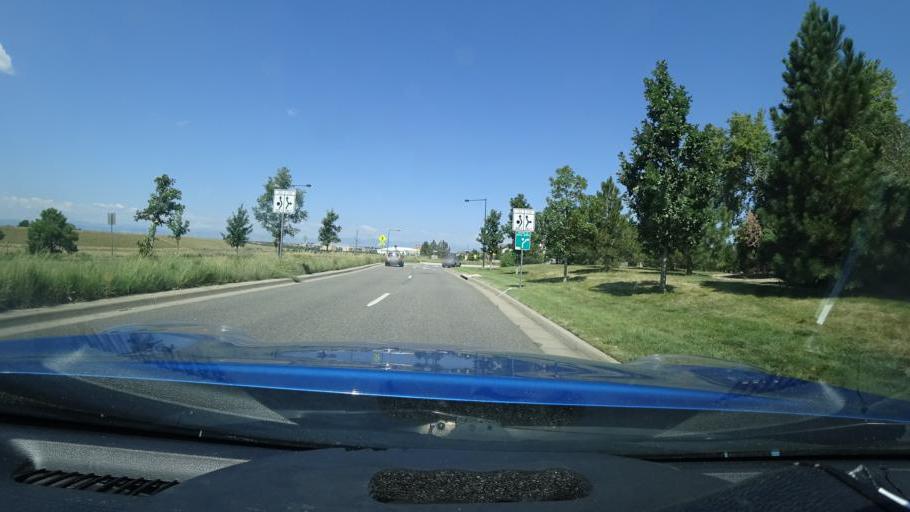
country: US
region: Colorado
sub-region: Adams County
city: Aurora
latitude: 39.7184
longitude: -104.8748
